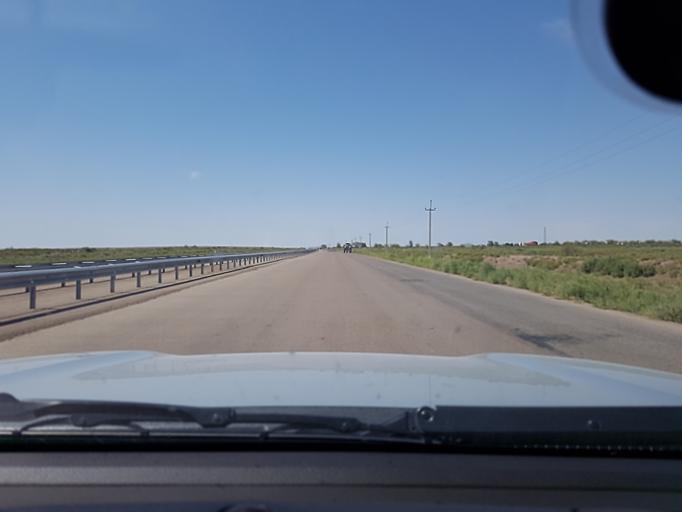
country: TM
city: Akdepe
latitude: 41.7404
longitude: 59.2243
